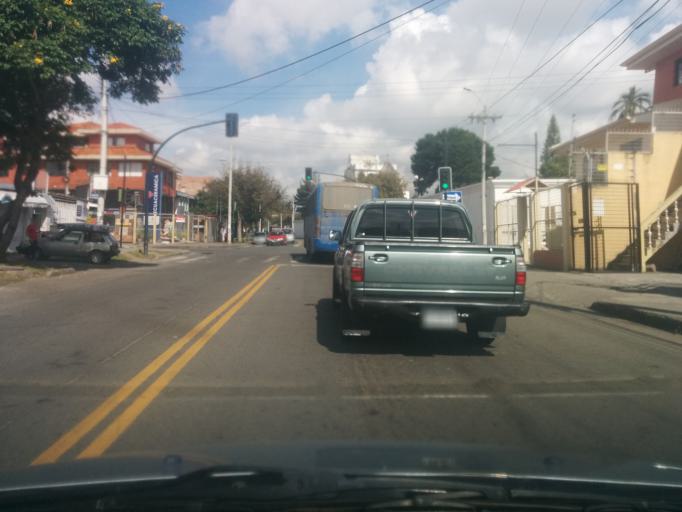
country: EC
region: Azuay
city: Cuenca
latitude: -2.8992
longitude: -78.9902
